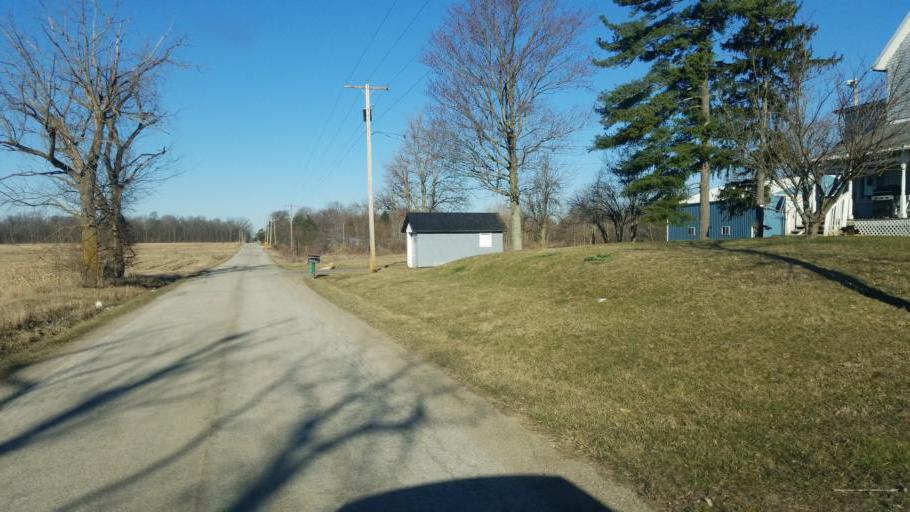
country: US
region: Ohio
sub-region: Morrow County
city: Mount Gilead
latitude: 40.5861
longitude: -82.8638
